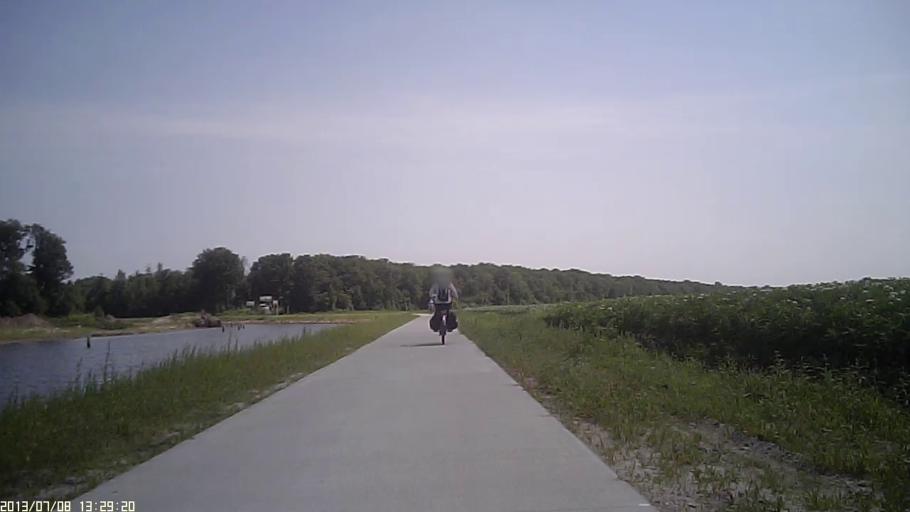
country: NL
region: Drenthe
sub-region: Gemeente Emmen
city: Klazienaveen
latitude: 52.7438
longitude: 6.9857
